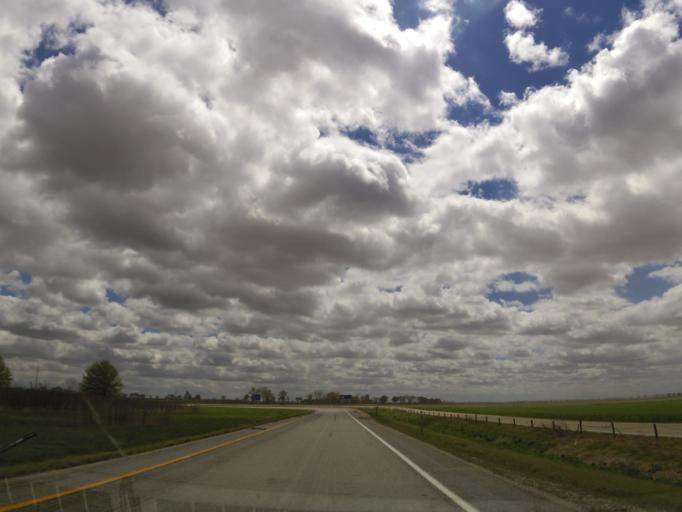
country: US
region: Arkansas
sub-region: Poinsett County
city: Trumann
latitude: 35.6304
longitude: -90.5023
